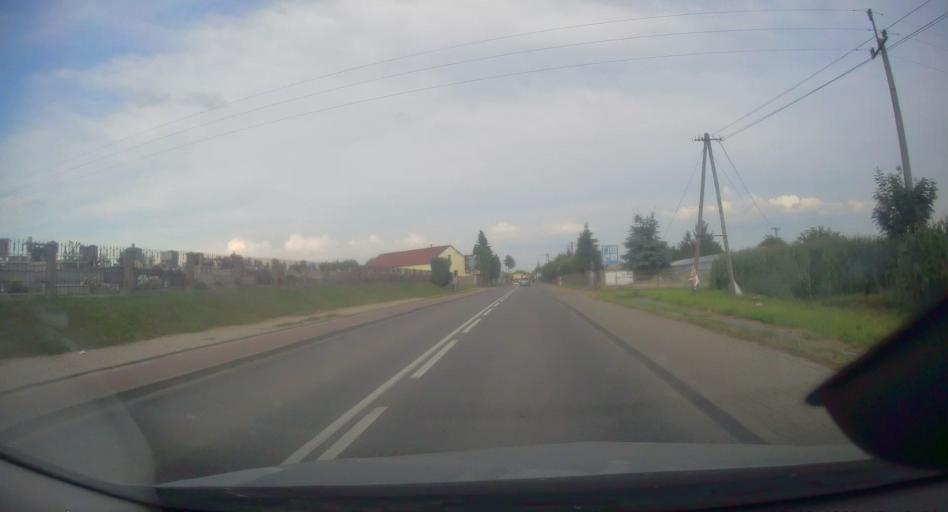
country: PL
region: Lesser Poland Voivodeship
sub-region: Powiat brzeski
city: Szczurowa
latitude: 50.1648
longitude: 20.5797
